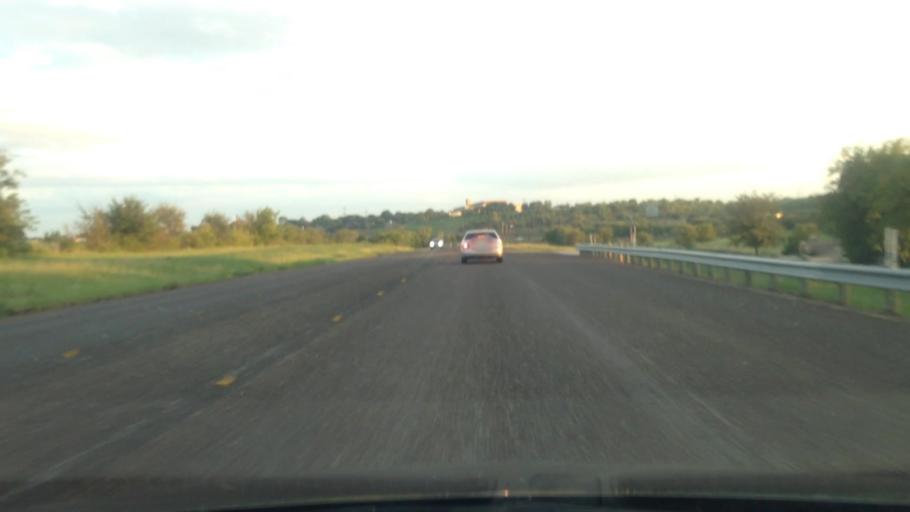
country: US
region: Texas
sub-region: Tarrant County
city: Benbrook
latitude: 32.6829
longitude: -97.4991
